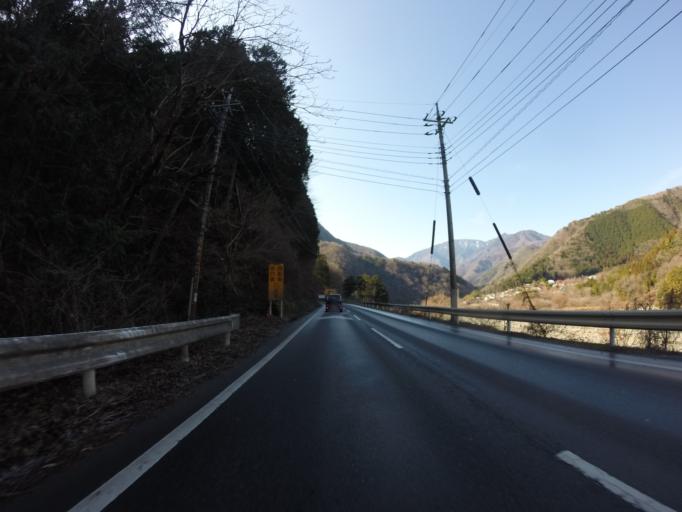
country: JP
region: Yamanashi
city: Ryuo
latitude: 35.4122
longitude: 138.3739
